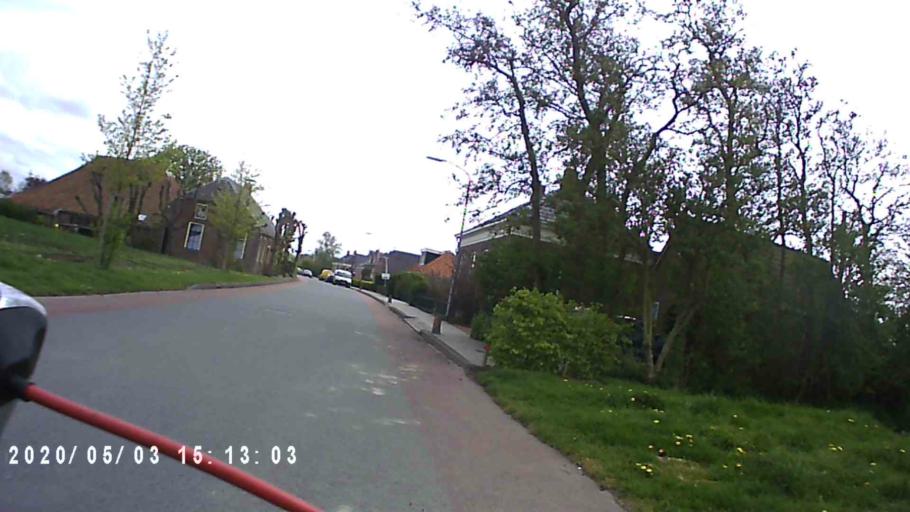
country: NL
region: Groningen
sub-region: Gemeente Winsum
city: Winsum
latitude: 53.3680
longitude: 6.4545
